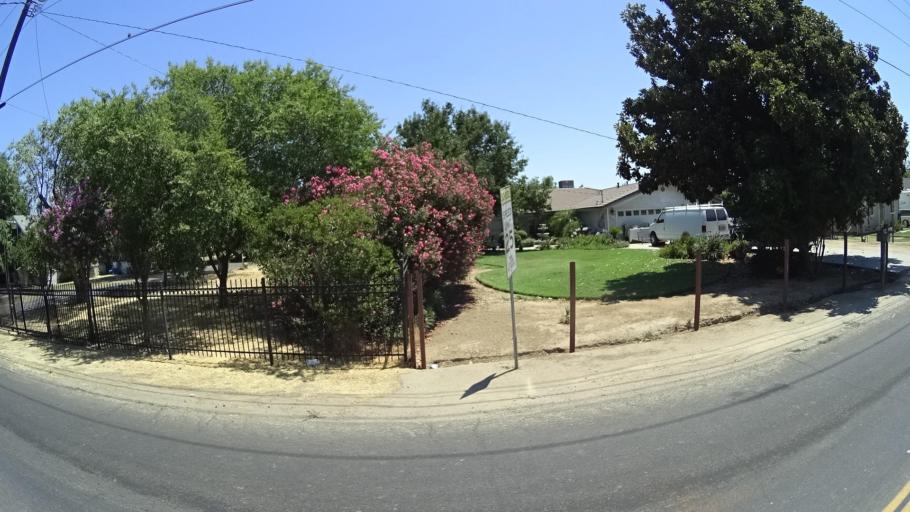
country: US
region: California
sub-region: Fresno County
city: Sunnyside
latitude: 36.7137
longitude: -119.7275
